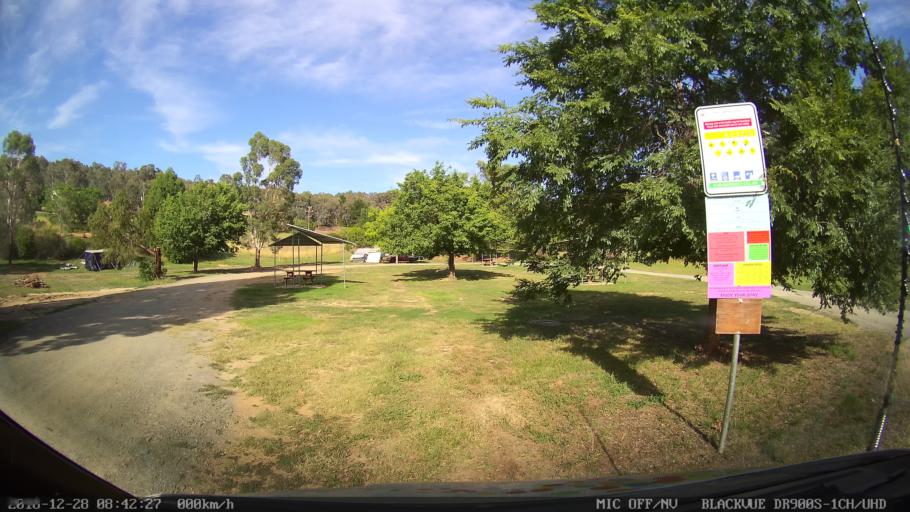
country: AU
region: New South Wales
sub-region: Upper Lachlan Shire
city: Crookwell
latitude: -34.0147
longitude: 149.3272
